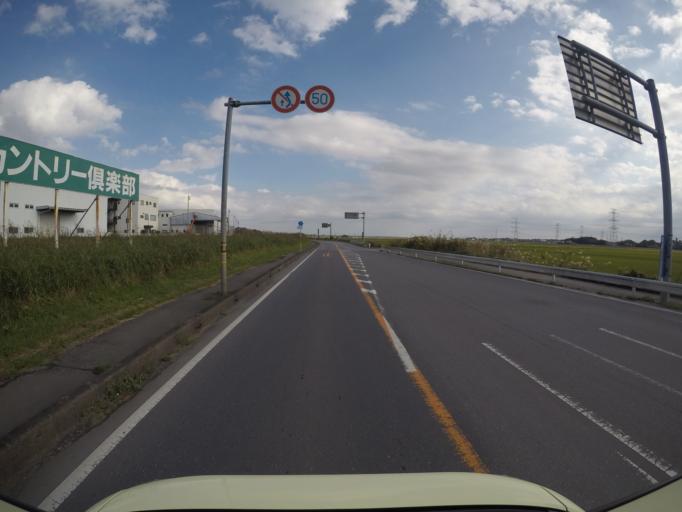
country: JP
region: Ibaraki
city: Iwai
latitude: 35.9919
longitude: 139.9015
